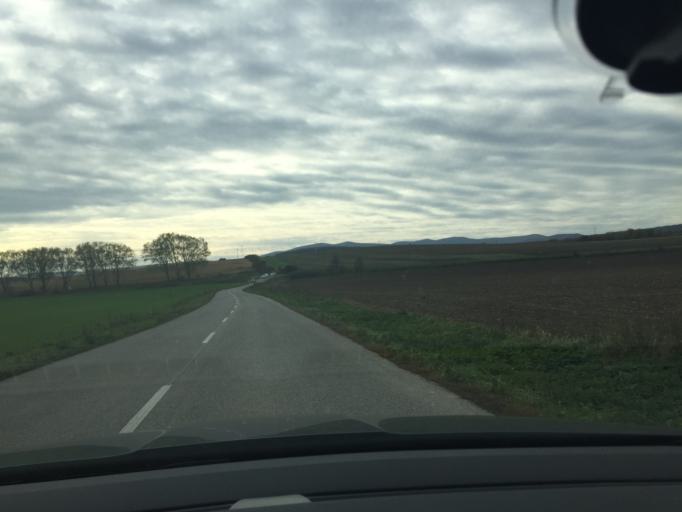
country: SK
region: Kosicky
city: Kosice
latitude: 48.8164
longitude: 21.3044
